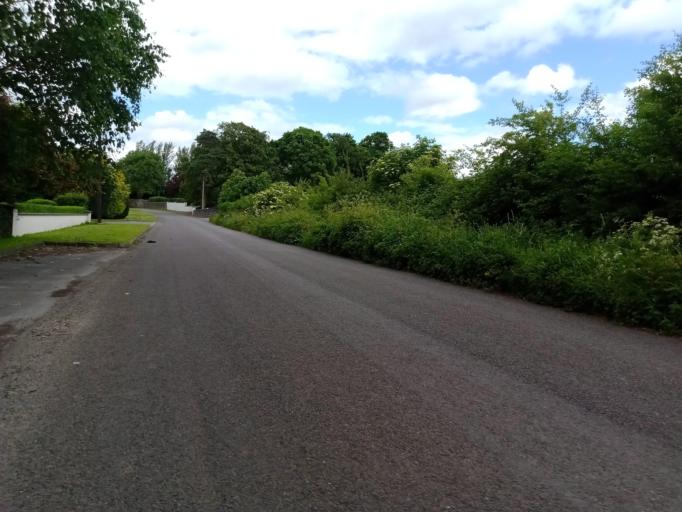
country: IE
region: Leinster
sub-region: Kilkenny
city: Kilkenny
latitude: 52.6832
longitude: -7.2489
